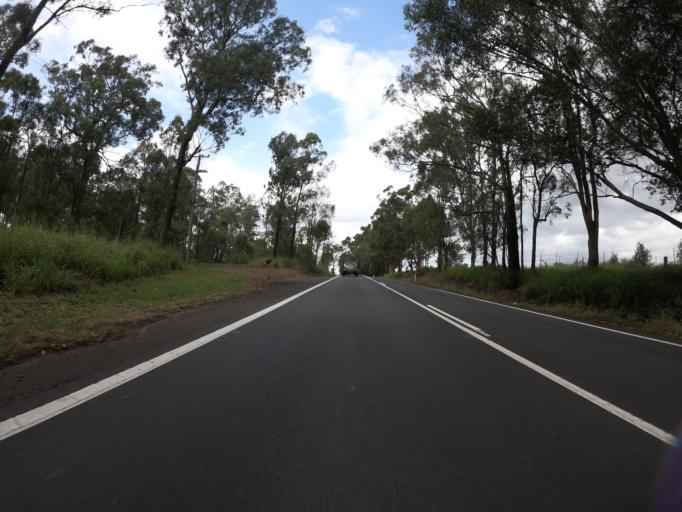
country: AU
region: New South Wales
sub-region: Blacktown
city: Riverstone
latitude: -33.6657
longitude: 150.8875
